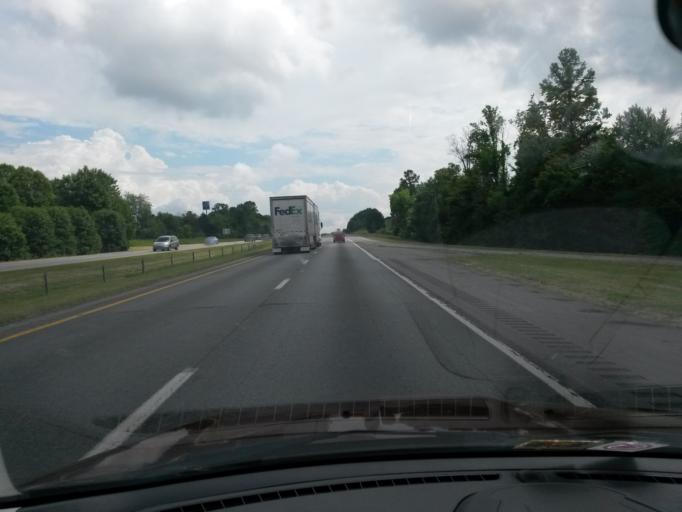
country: US
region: North Carolina
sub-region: Yadkin County
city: Jonesville
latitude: 36.1961
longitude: -80.8117
